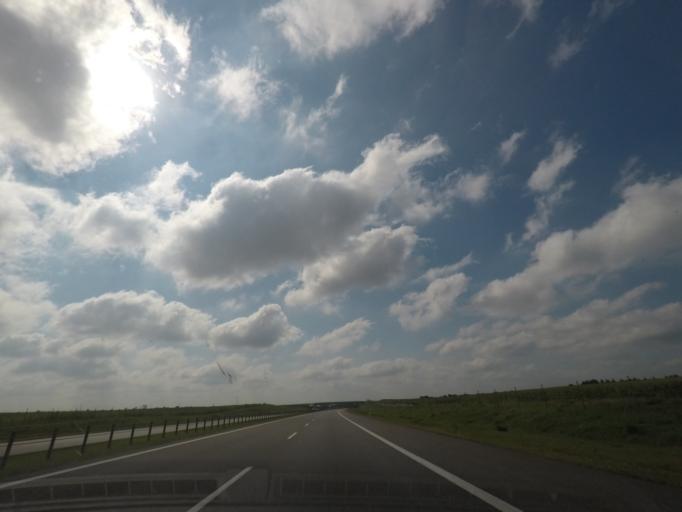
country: PL
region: Kujawsko-Pomorskie
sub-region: Powiat wabrzeski
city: Pluznica
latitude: 53.2161
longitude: 18.7362
